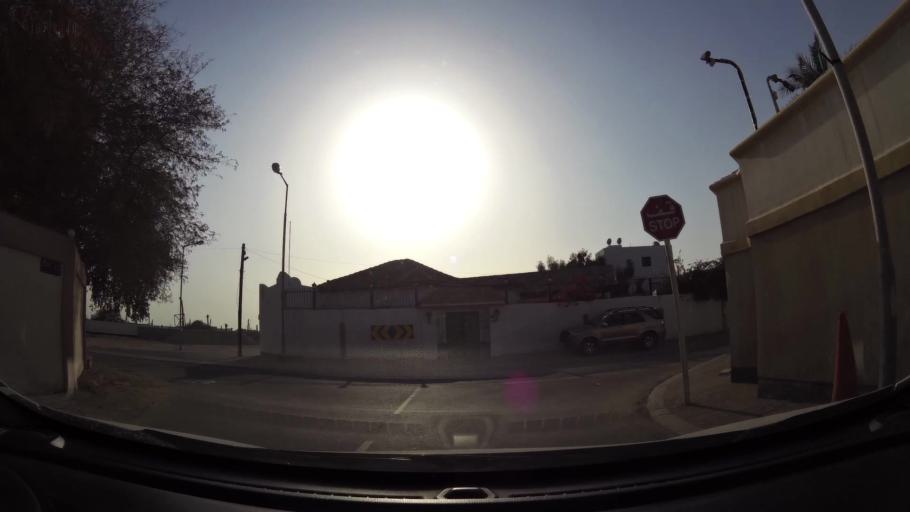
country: BH
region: Manama
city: Jidd Hafs
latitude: 26.2153
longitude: 50.4969
